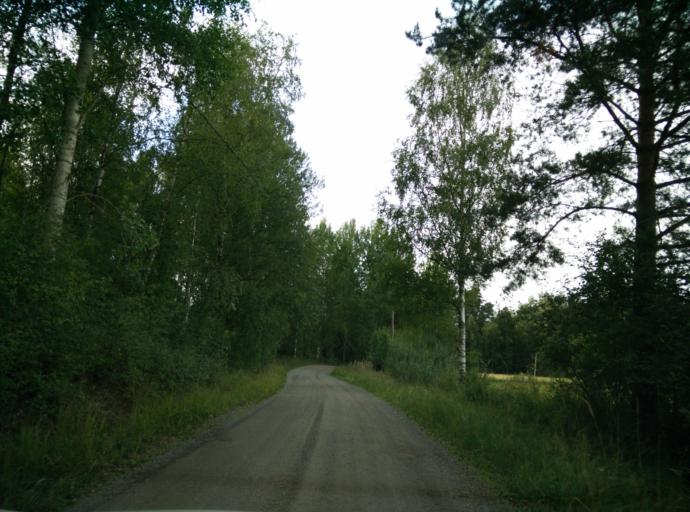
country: FI
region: Haeme
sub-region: Haemeenlinna
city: Kalvola
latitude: 61.1210
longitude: 24.1417
